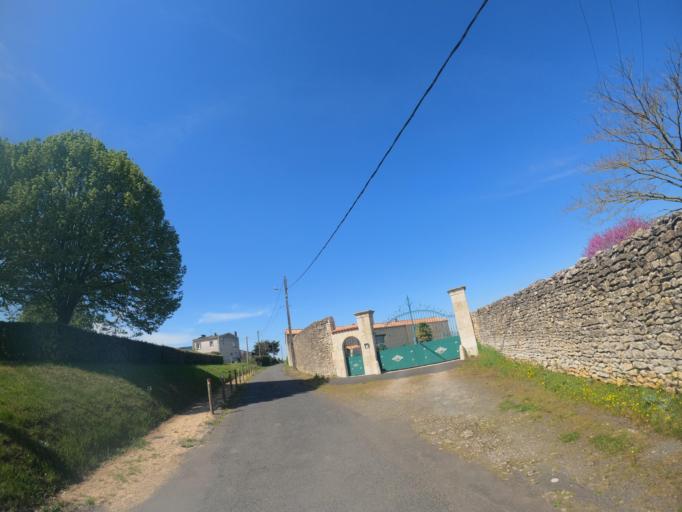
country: FR
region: Poitou-Charentes
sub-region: Departement des Deux-Sevres
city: Airvault
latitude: 46.8854
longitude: -0.1444
